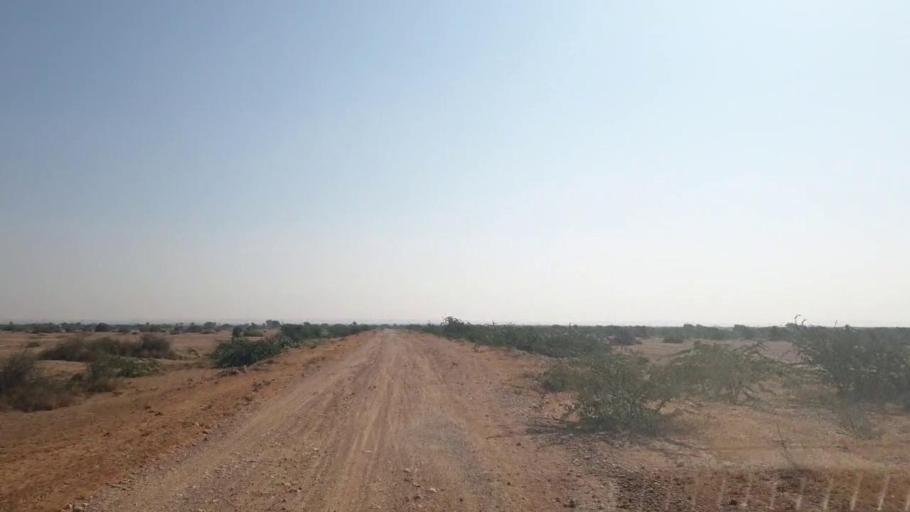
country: PK
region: Sindh
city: Gharo
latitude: 25.1424
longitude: 67.7292
